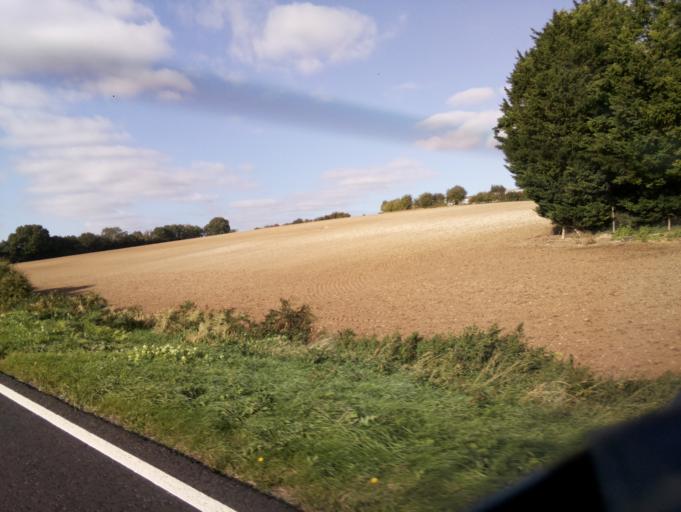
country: GB
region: England
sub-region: Hampshire
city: Four Marks
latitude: 51.1708
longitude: -1.0454
